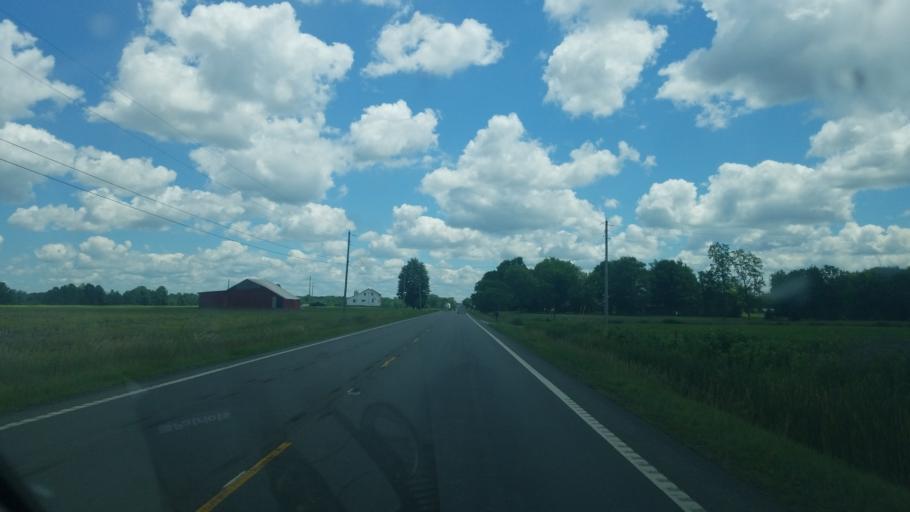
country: US
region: Ohio
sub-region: Huron County
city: New London
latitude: 41.0296
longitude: -82.3794
